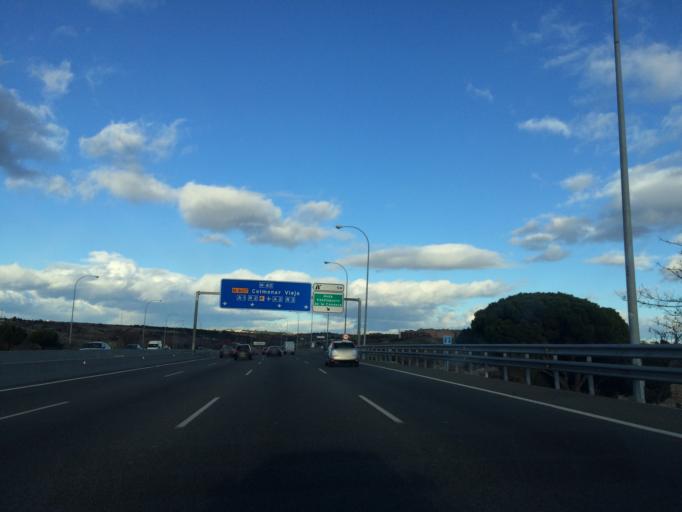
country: ES
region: Madrid
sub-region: Provincia de Madrid
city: Fuencarral-El Pardo
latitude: 40.4973
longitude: -3.7249
